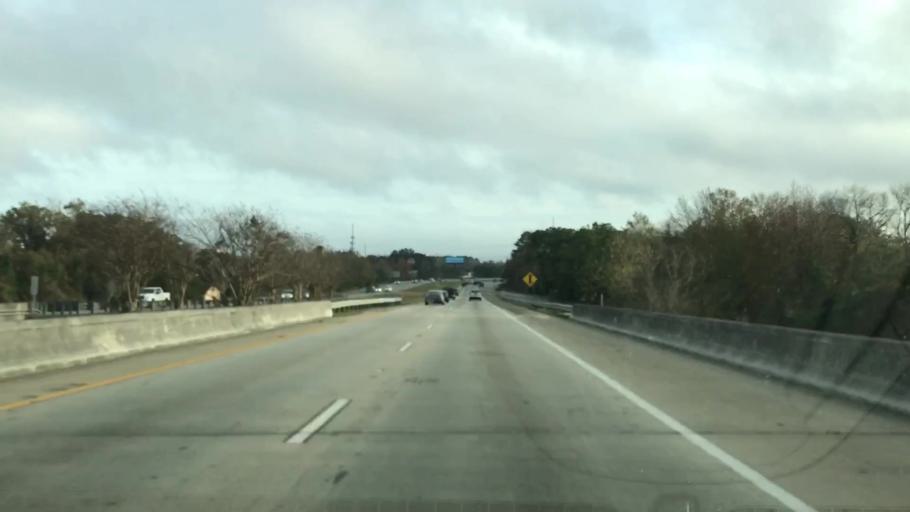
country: US
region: South Carolina
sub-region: Charleston County
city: North Charleston
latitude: 32.8526
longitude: -80.0205
